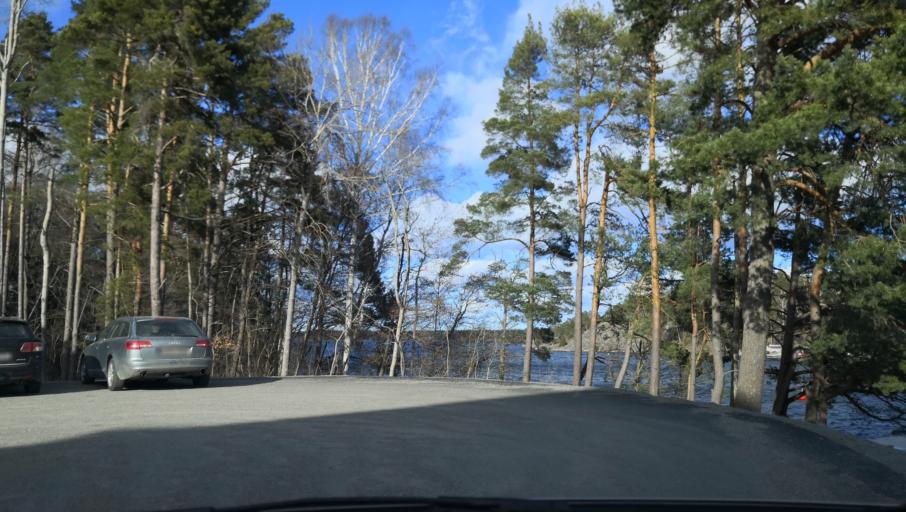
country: SE
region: Stockholm
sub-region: Varmdo Kommun
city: Mortnas
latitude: 59.3154
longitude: 18.4584
